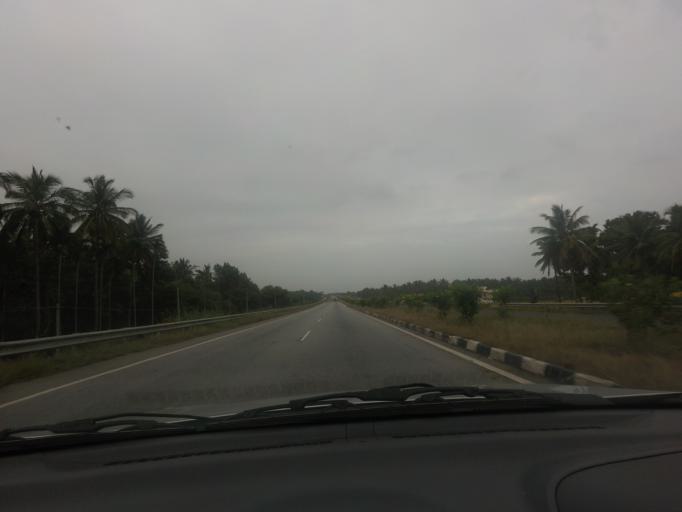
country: IN
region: Karnataka
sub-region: Tumkur
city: Kunigal
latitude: 13.0203
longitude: 77.0518
